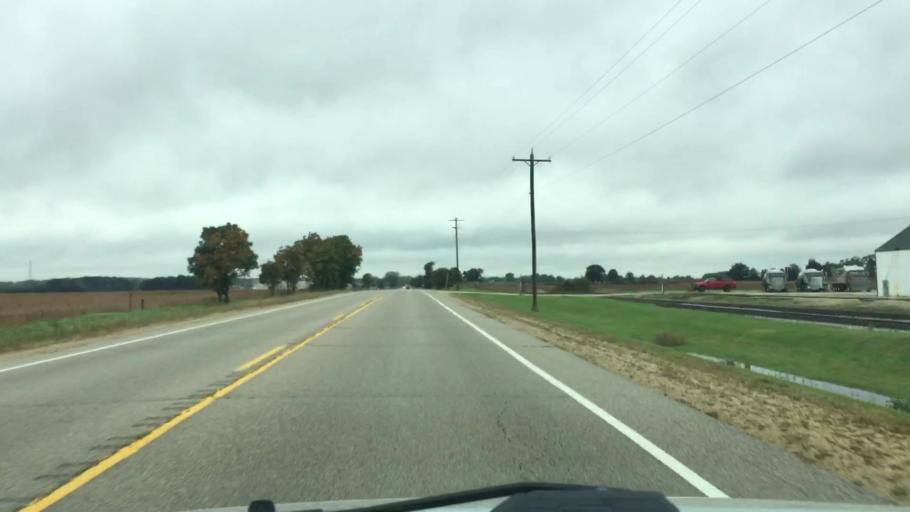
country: US
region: Wisconsin
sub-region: Walworth County
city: Whitewater
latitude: 42.8024
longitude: -88.7932
